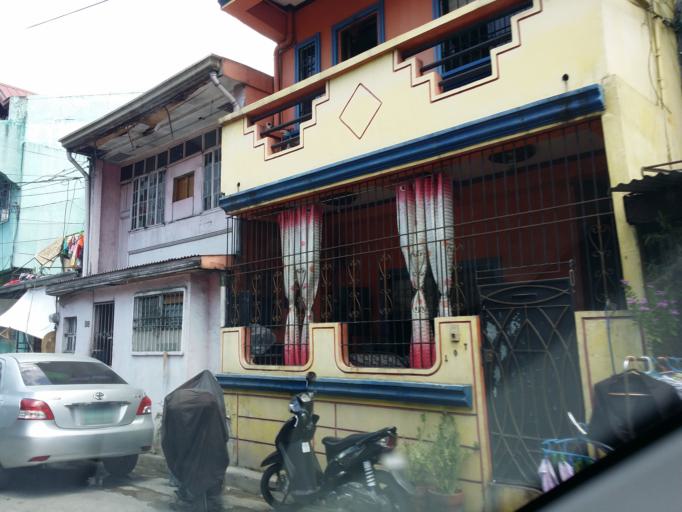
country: PH
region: Metro Manila
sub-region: Mandaluyong
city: Mandaluyong City
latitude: 14.5790
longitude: 121.0375
